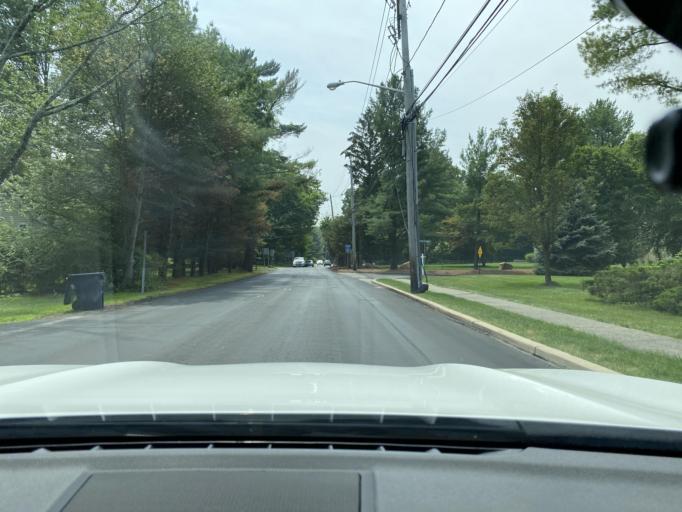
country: US
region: New York
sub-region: Rockland County
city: Airmont
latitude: 41.0955
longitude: -74.1198
